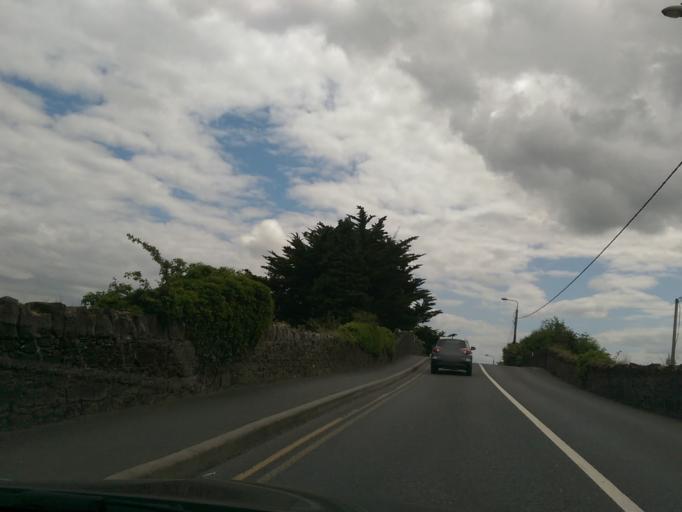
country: IE
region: Munster
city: Thurles
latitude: 52.6826
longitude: -7.8214
